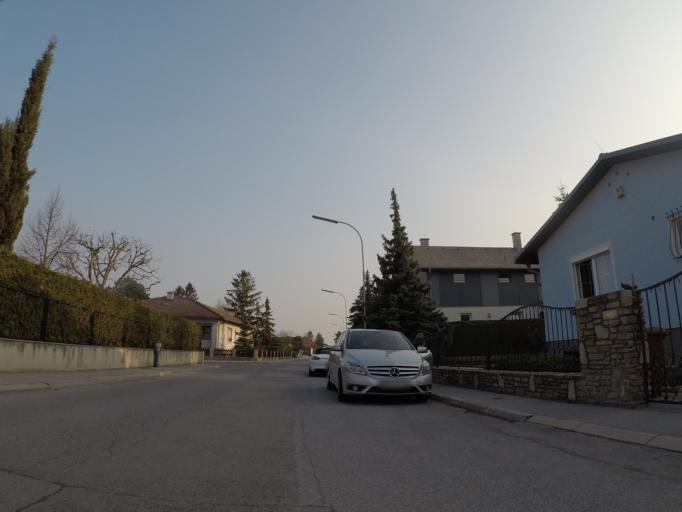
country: AT
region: Lower Austria
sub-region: Politischer Bezirk Modling
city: Wiener Neudorf
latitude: 48.0905
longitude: 16.3237
